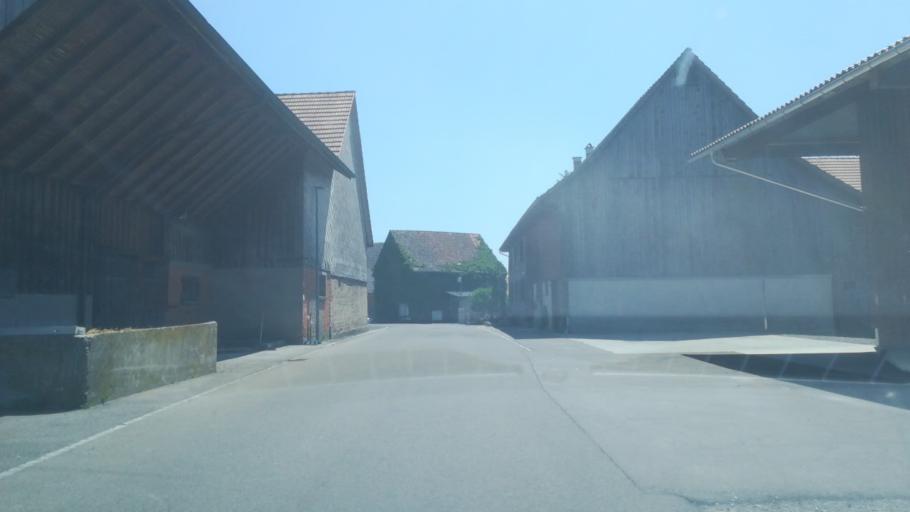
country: CH
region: Thurgau
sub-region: Kreuzlingen District
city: Ermatingen
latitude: 47.6363
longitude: 9.0760
